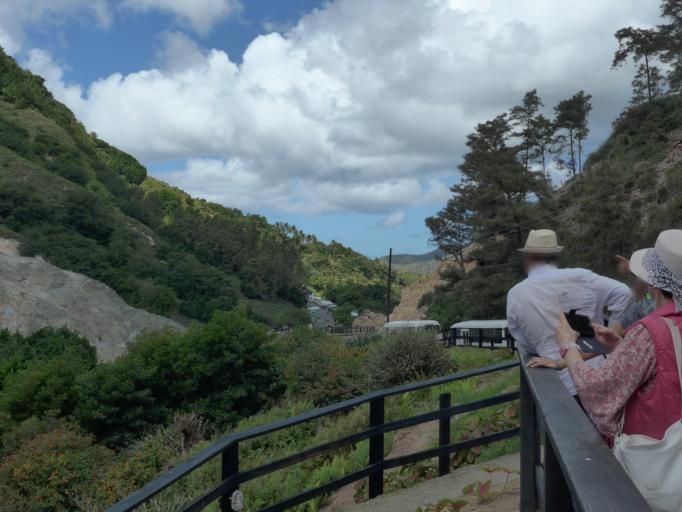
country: LC
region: Soufriere
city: Soufriere
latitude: 13.8389
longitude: -61.0462
